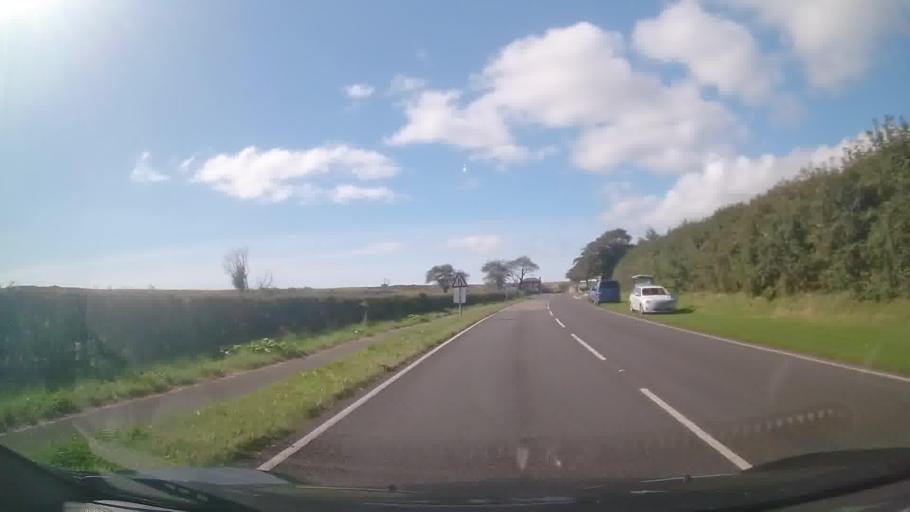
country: GB
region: Wales
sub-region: Pembrokeshire
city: Penally
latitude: 51.6605
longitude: -4.7207
